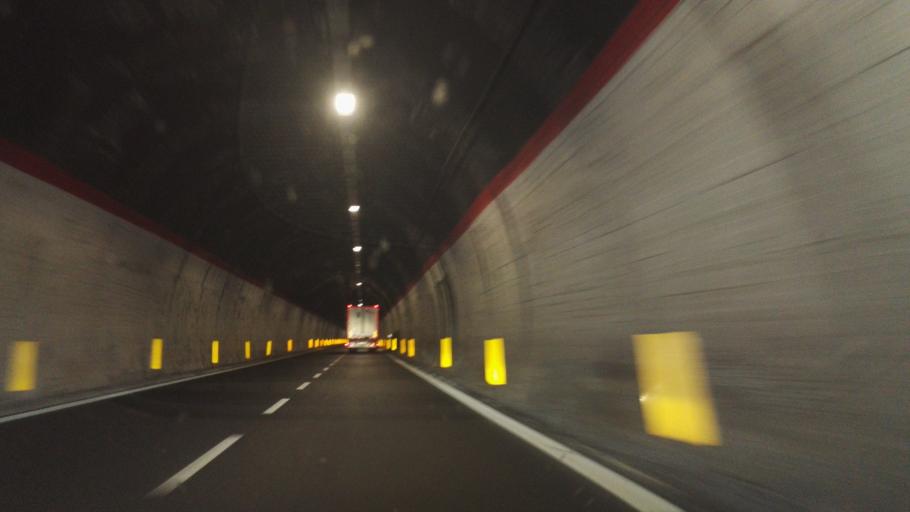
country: IT
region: Calabria
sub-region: Provincia di Cosenza
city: Laurignano
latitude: 39.2859
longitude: 16.2415
